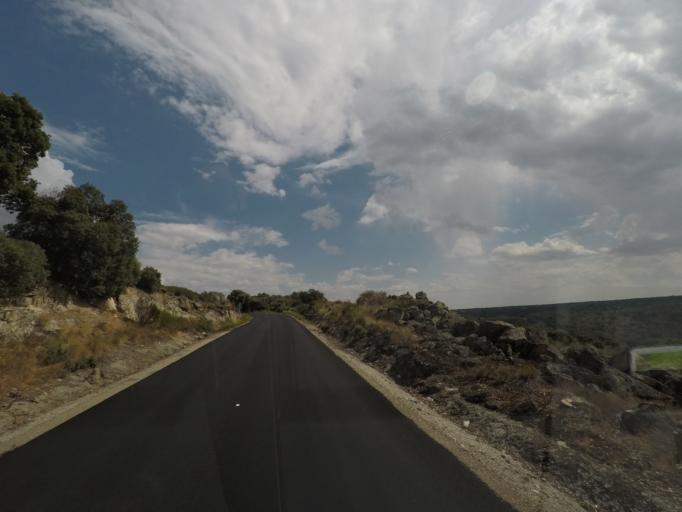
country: ES
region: Castille and Leon
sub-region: Provincia de Salamanca
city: Almendra
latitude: 41.2764
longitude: -6.3295
